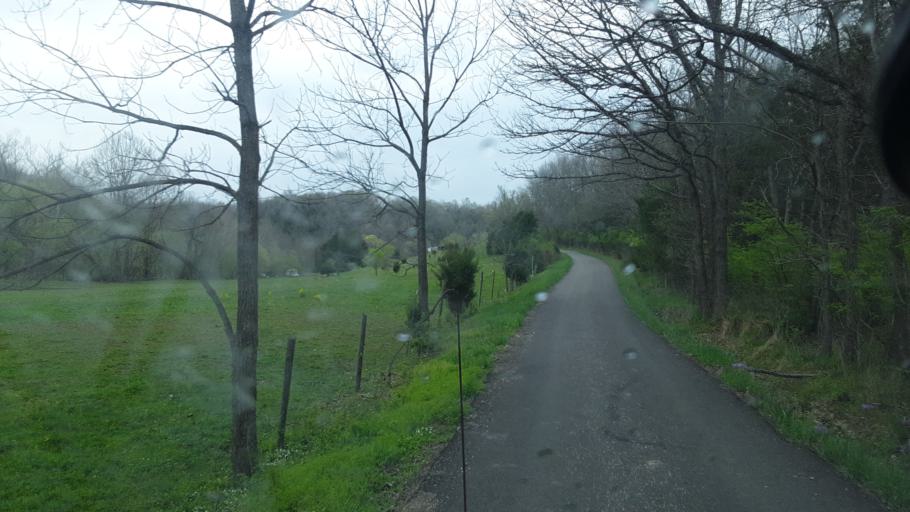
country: US
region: Kentucky
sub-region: Owen County
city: Owenton
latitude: 38.6718
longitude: -84.7952
